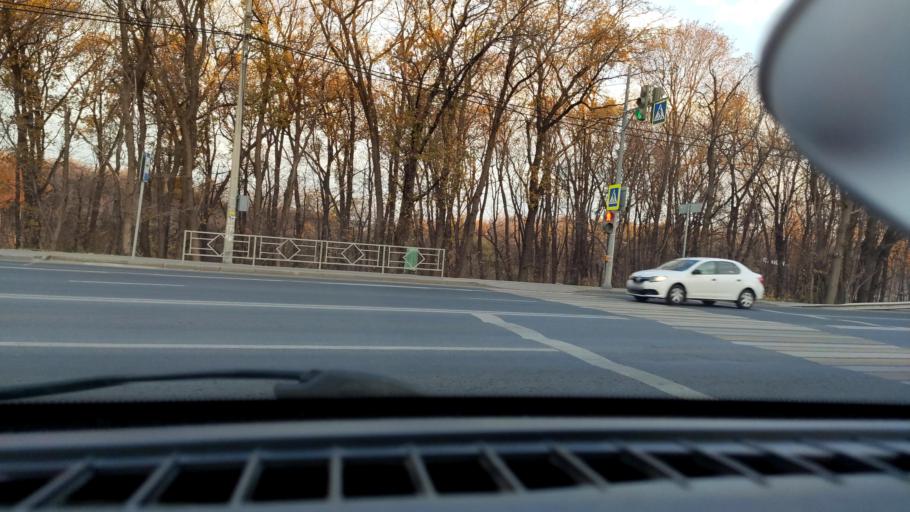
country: RU
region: Samara
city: Samara
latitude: 53.2730
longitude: 50.2254
